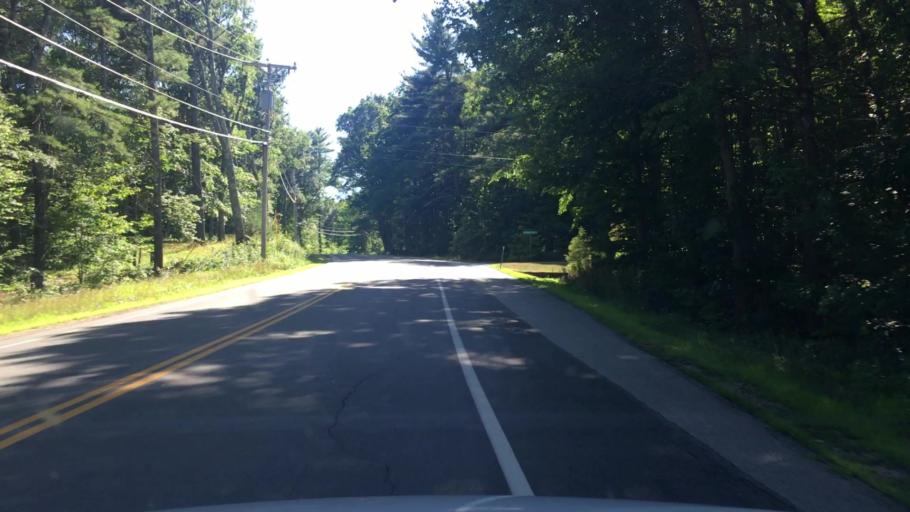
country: US
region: New Hampshire
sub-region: Rockingham County
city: Newmarket
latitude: 43.0342
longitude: -70.9563
